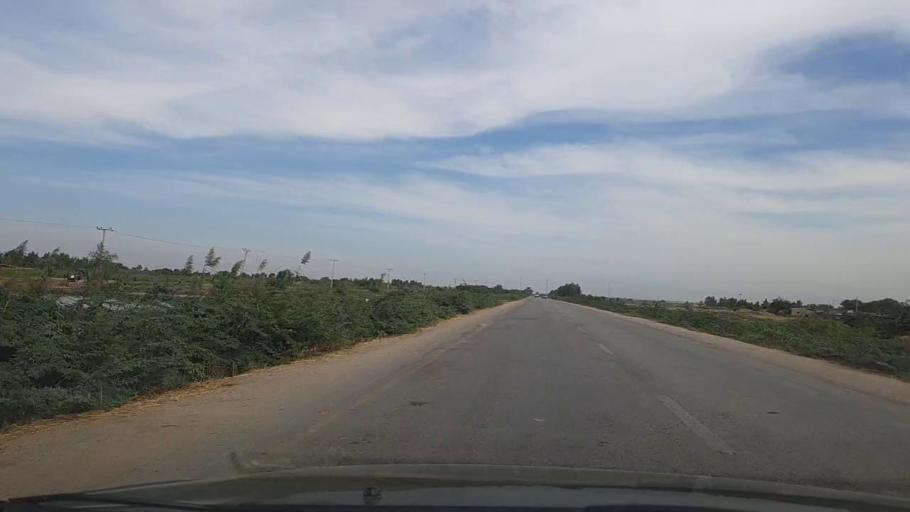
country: PK
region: Sindh
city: Thatta
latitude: 24.7974
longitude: 67.9621
